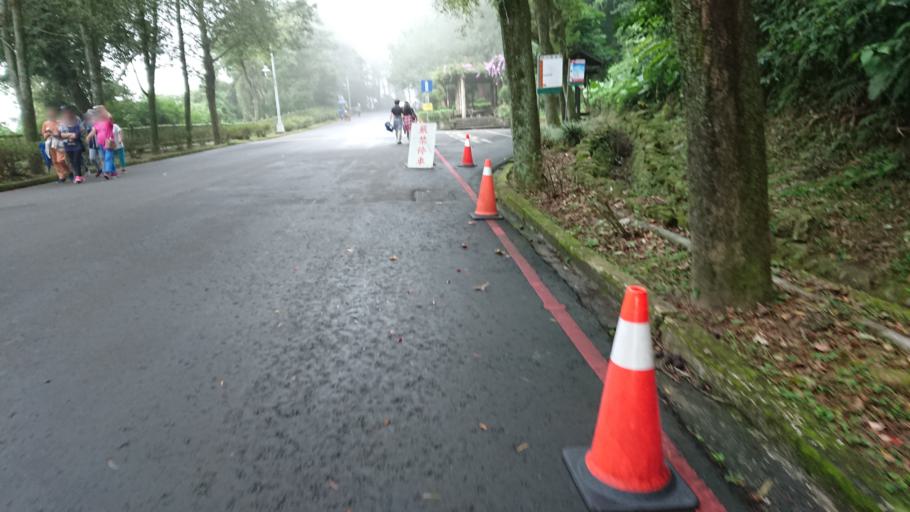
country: TW
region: Taiwan
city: Daxi
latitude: 24.8156
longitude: 121.2413
